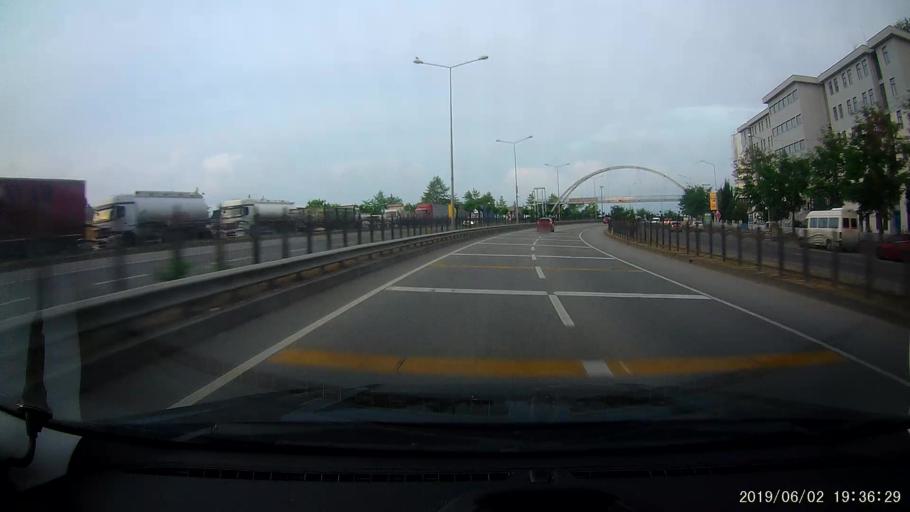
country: TR
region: Giresun
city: Giresun
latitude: 40.9239
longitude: 38.3890
